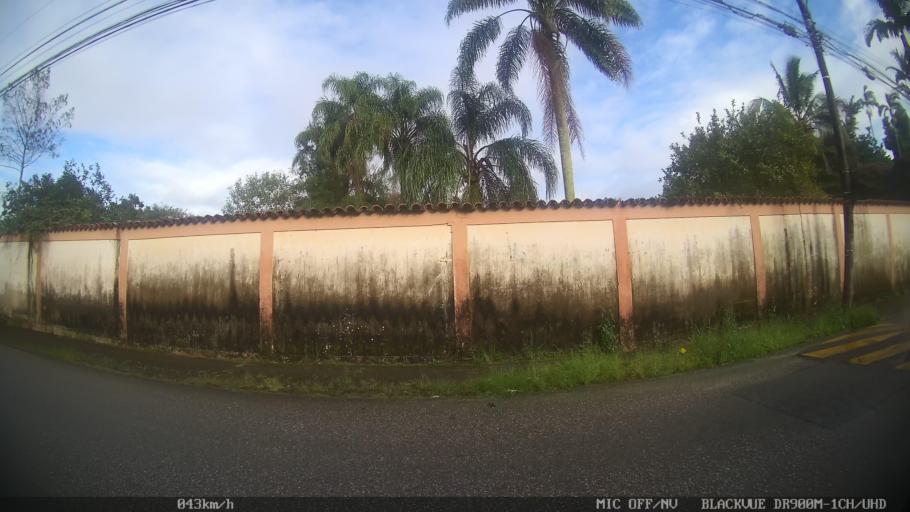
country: BR
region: Santa Catarina
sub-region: Sao Jose
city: Campinas
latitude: -27.6111
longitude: -48.6314
